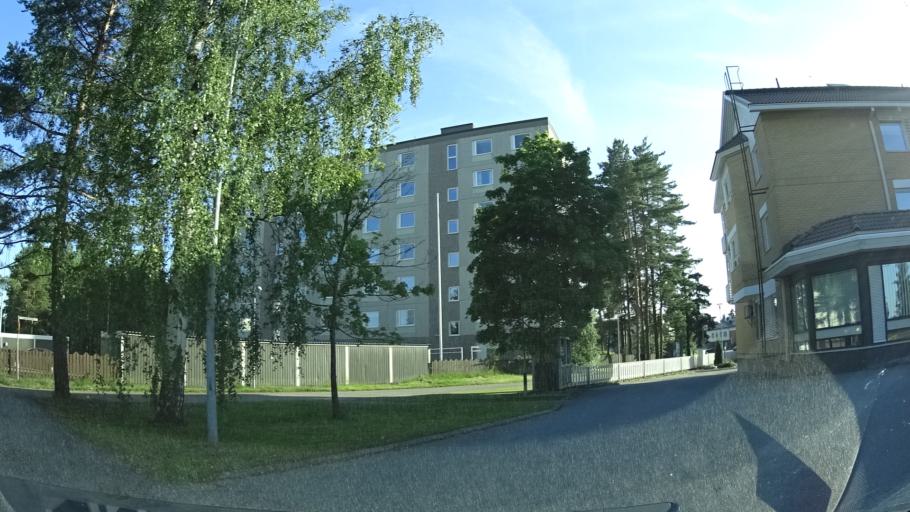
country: FI
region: Satakunta
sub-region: Pori
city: Harjavalta
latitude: 61.3149
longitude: 22.1489
